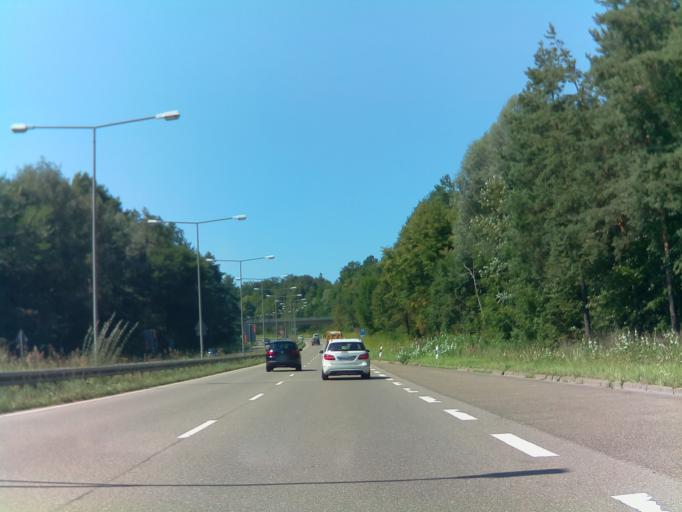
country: DE
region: Baden-Wuerttemberg
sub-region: Regierungsbezirk Stuttgart
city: Gerlingen
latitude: 48.7808
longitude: 9.0853
